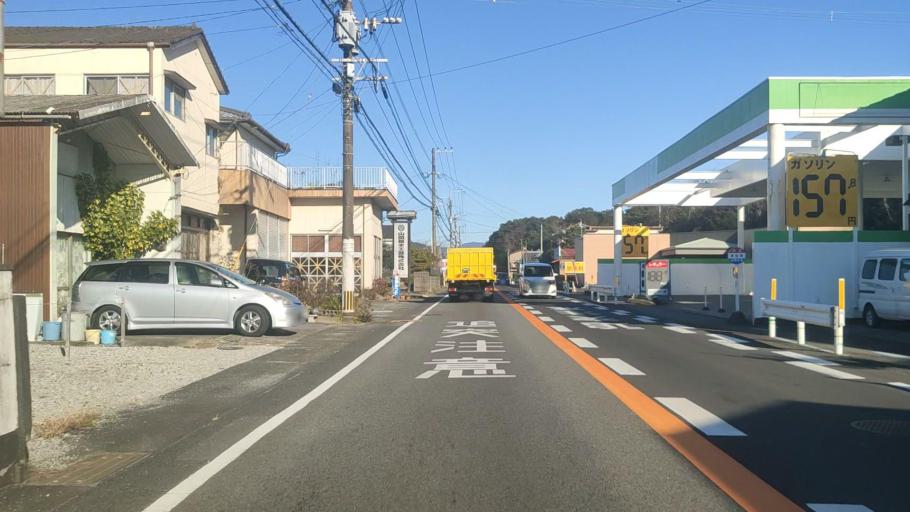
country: JP
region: Miyazaki
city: Nobeoka
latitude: 32.5245
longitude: 131.6829
